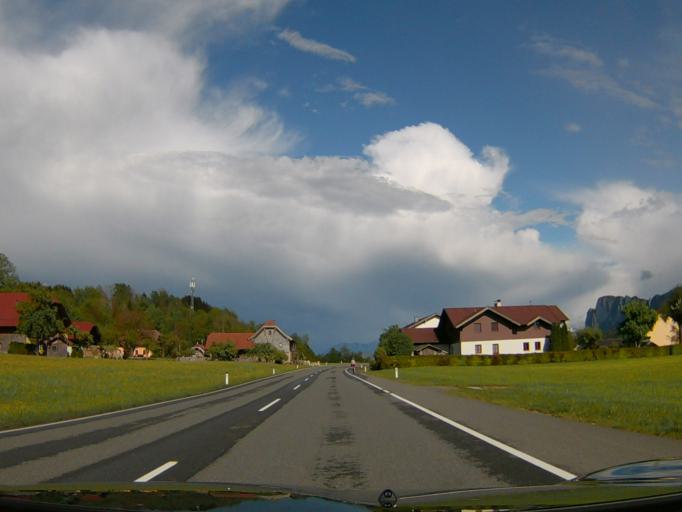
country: AT
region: Salzburg
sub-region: Politischer Bezirk Salzburg-Umgebung
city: Thalgau
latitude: 47.8430
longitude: 13.2627
